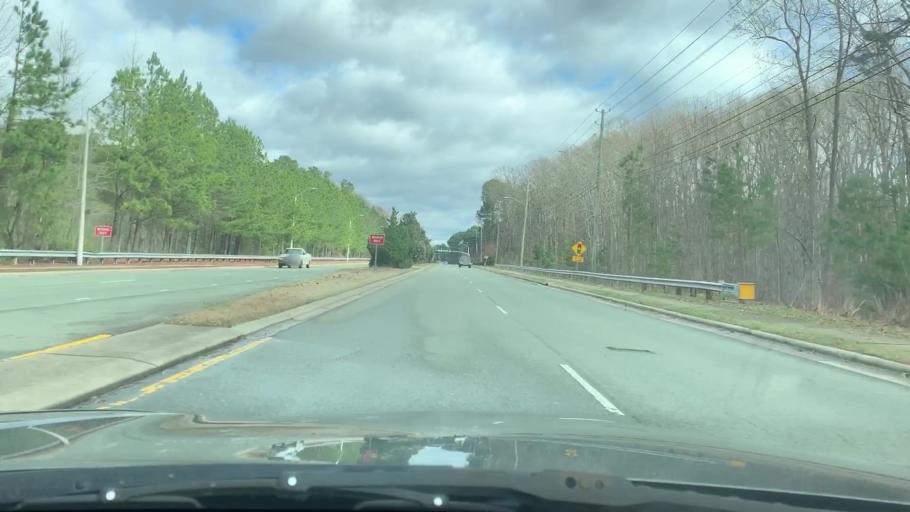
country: US
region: North Carolina
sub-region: Wake County
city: Cary
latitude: 35.8145
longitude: -78.7759
